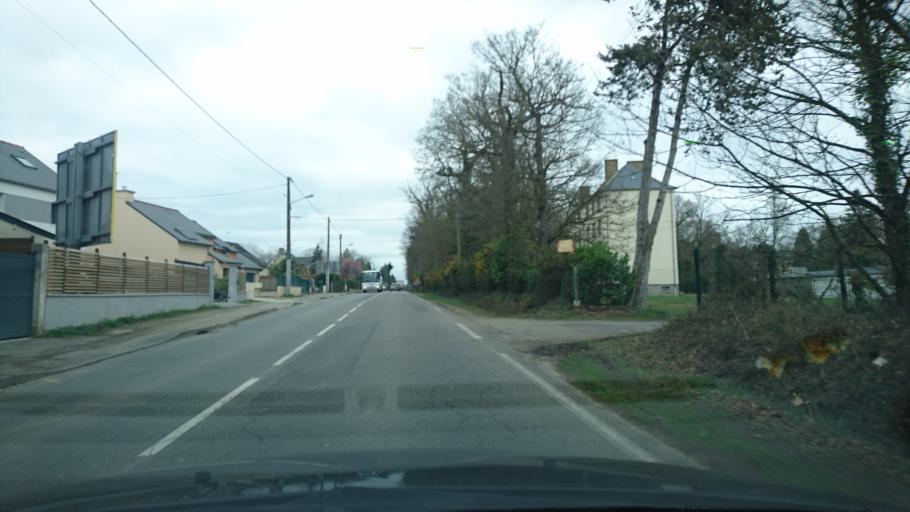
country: FR
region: Brittany
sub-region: Departement d'Ille-et-Vilaine
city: Bruz
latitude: 48.0327
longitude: -1.7517
